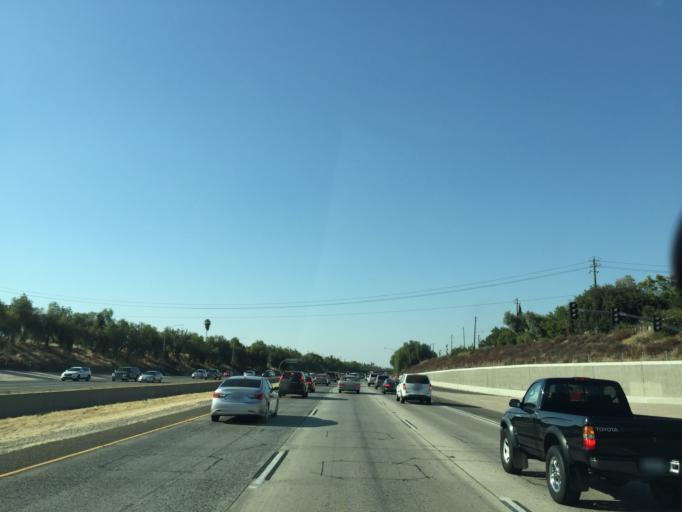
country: US
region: California
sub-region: Fresno County
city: Fresno
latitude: 36.7950
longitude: -119.7849
